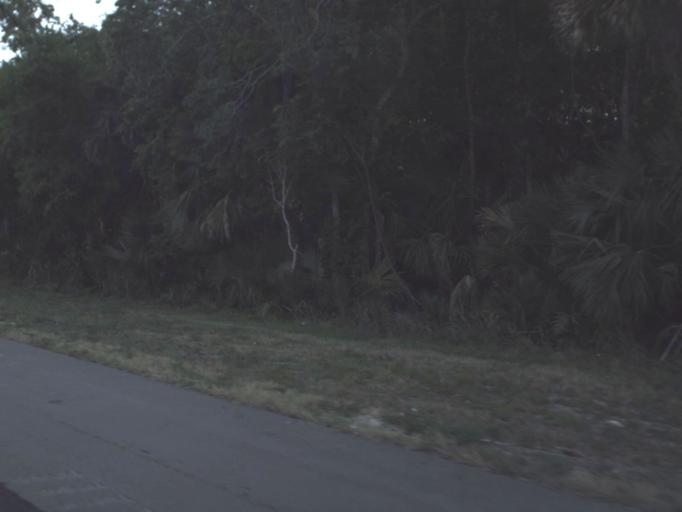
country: US
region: Florida
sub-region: Brevard County
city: Mims
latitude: 28.6976
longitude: -80.8828
